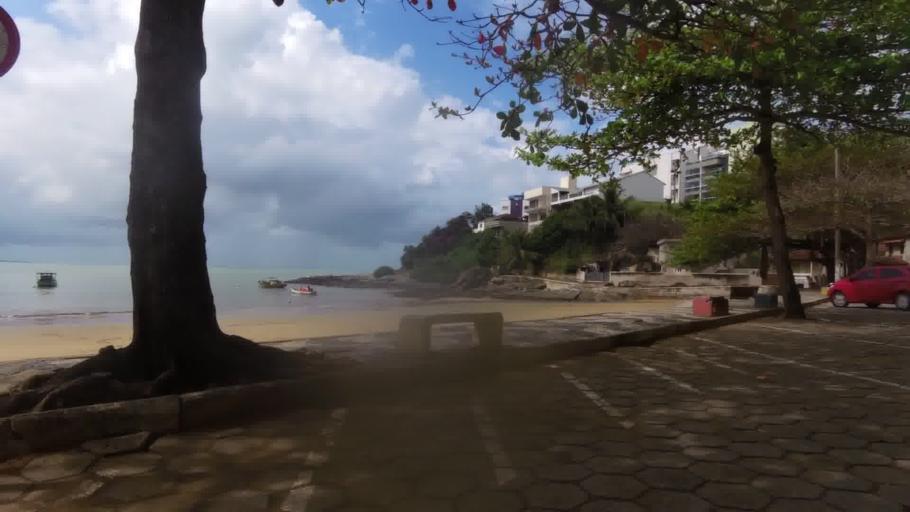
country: BR
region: Espirito Santo
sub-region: Piuma
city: Piuma
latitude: -20.8319
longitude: -40.6941
